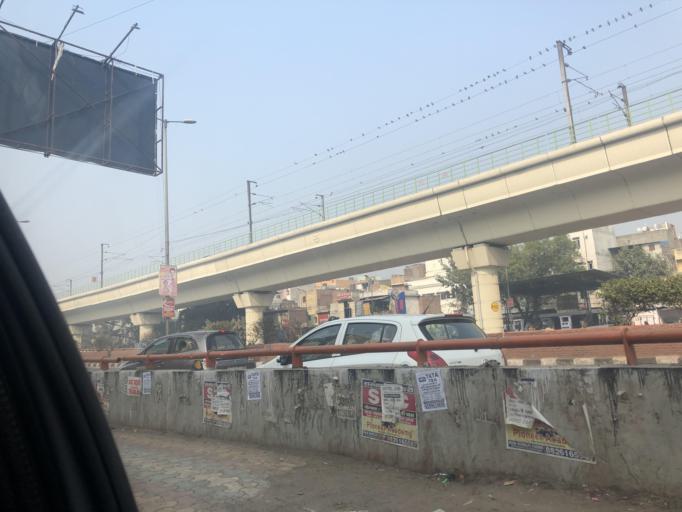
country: IN
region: NCT
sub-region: West Delhi
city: Nangloi Jat
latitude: 28.6821
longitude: 77.0708
